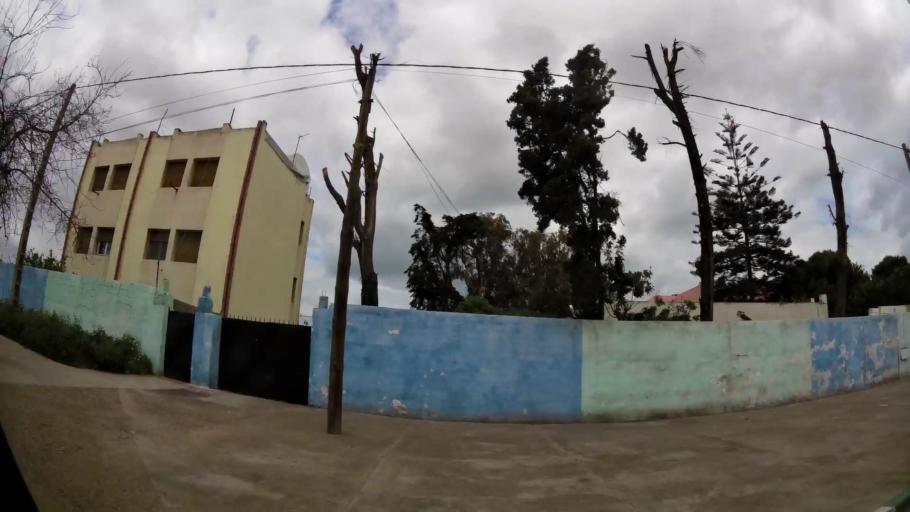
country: MA
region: Grand Casablanca
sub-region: Casablanca
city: Casablanca
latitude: 33.6047
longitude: -7.5534
